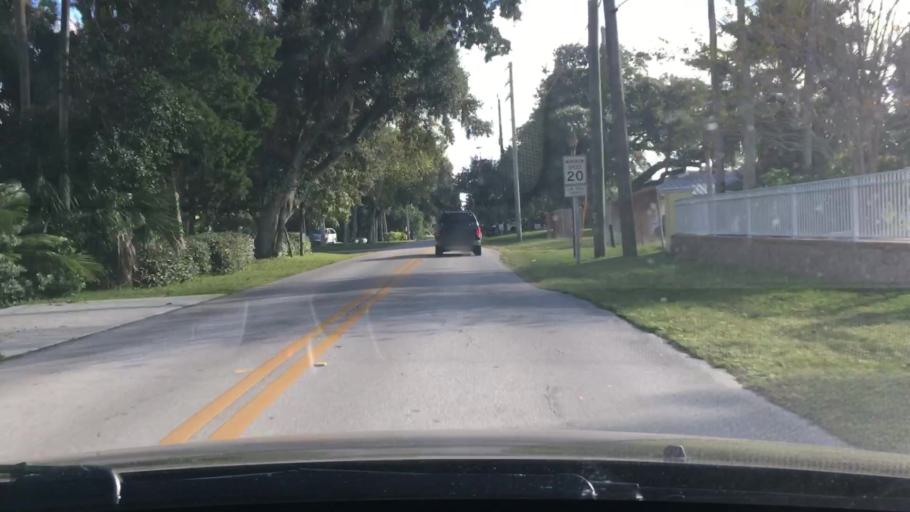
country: US
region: Florida
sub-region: Volusia County
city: Ormond-by-the-Sea
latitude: 29.3301
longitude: -81.0659
